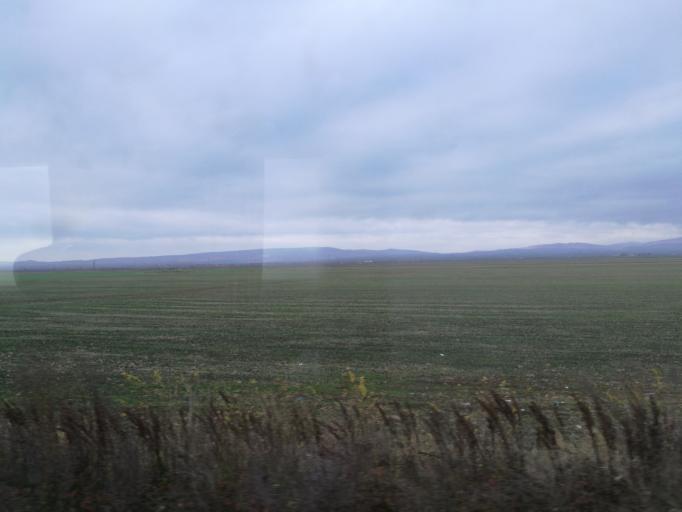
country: RO
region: Vrancea
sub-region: Comuna Gugesti
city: Gugesti
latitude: 45.6018
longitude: 27.1416
